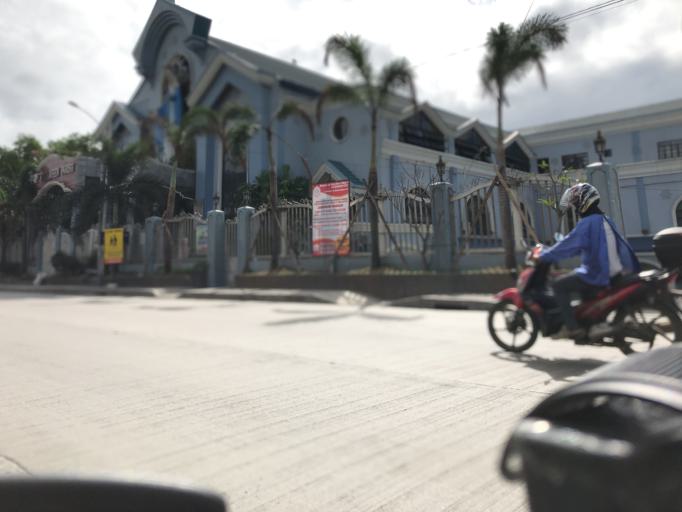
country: PH
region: Calabarzon
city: Bagong Pagasa
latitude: 14.7303
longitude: 121.0556
